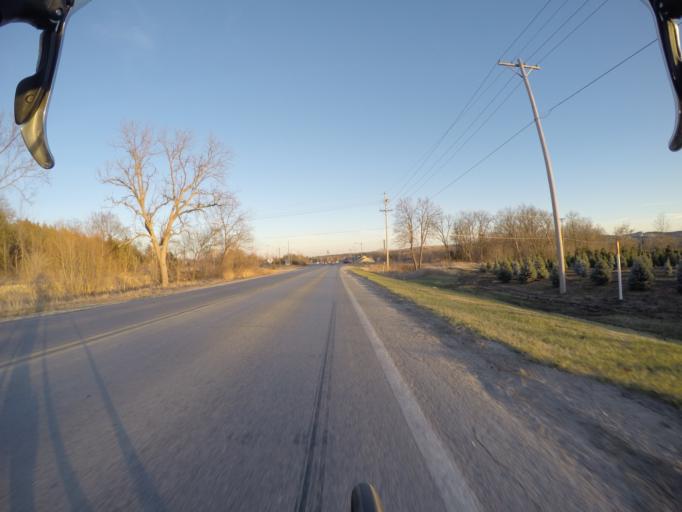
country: US
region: Kansas
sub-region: Riley County
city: Manhattan
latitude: 39.1927
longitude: -96.6426
